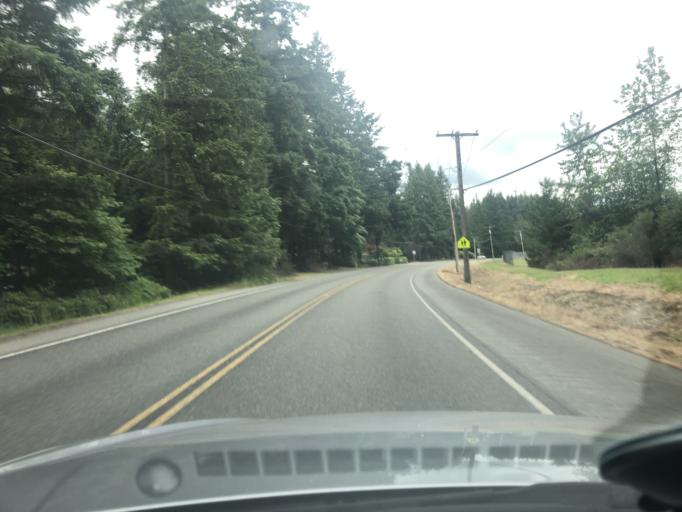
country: US
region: Washington
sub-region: King County
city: Black Diamond
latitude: 47.3258
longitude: -122.0403
